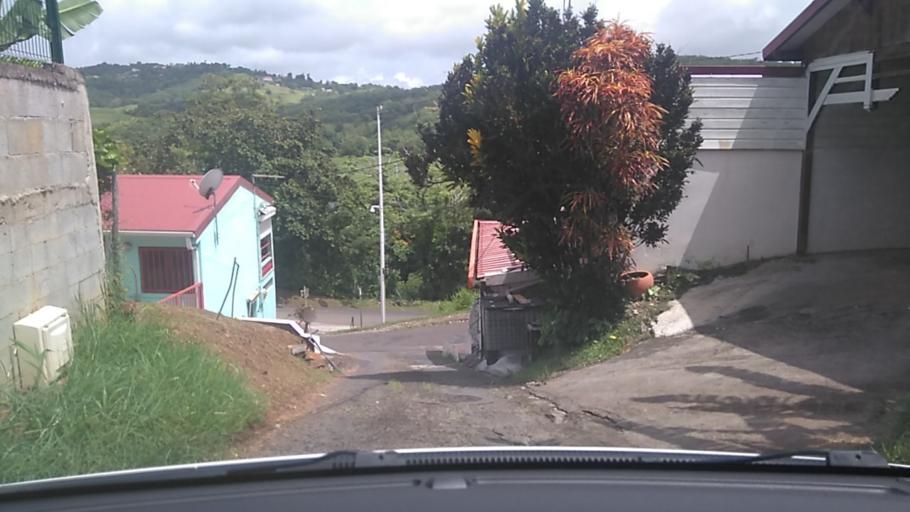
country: MQ
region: Martinique
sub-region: Martinique
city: Saint-Esprit
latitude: 14.5613
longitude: -60.9331
